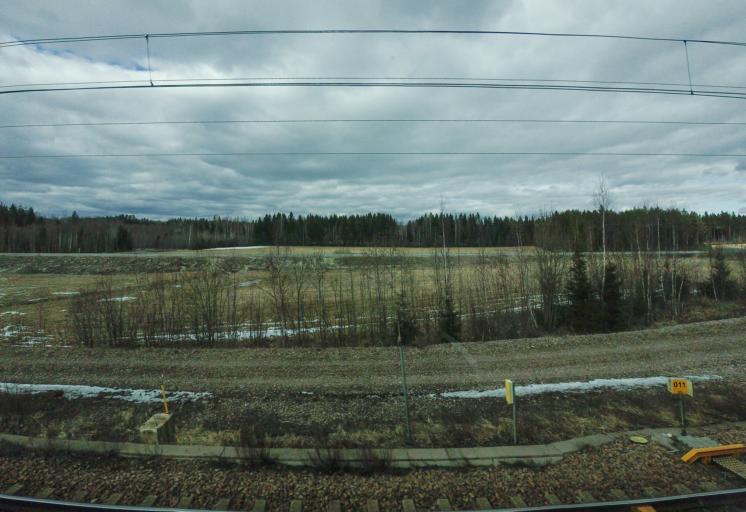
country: FI
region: South Karelia
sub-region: Lappeenranta
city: Lemi
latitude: 60.9421
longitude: 27.7462
